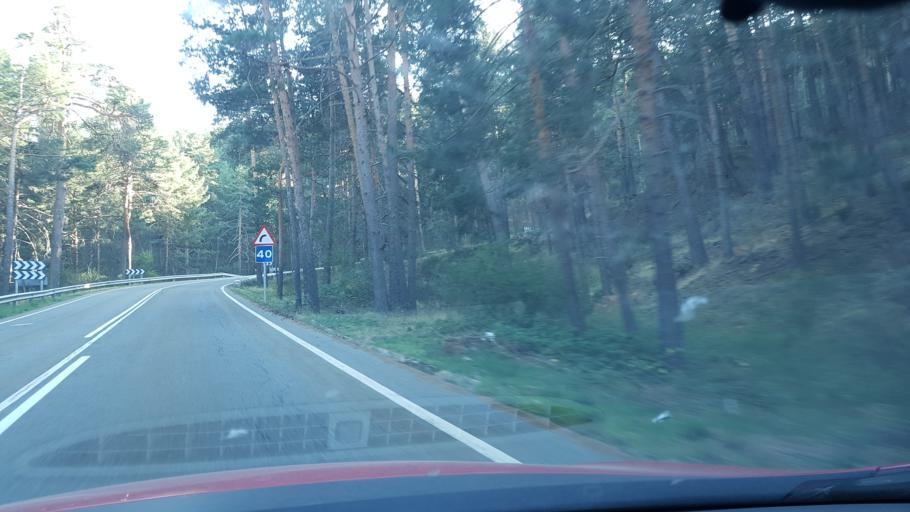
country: ES
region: Castille and Leon
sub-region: Provincia de Segovia
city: San Ildefonso
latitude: 40.8174
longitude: -4.0149
